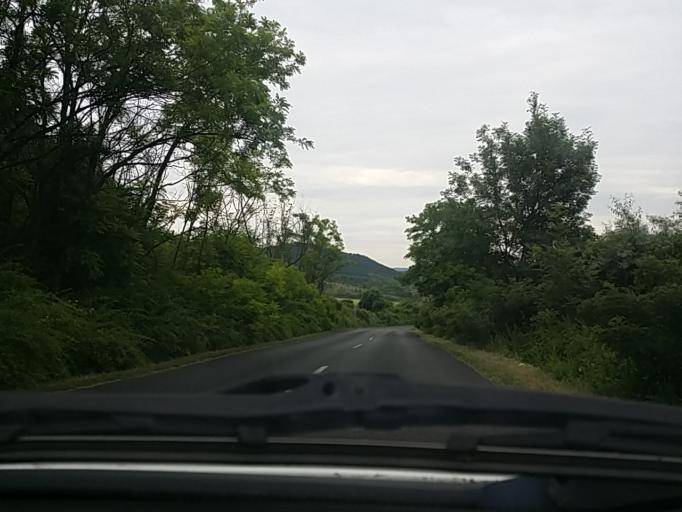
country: HU
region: Pest
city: Csobanka
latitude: 47.6368
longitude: 18.9544
